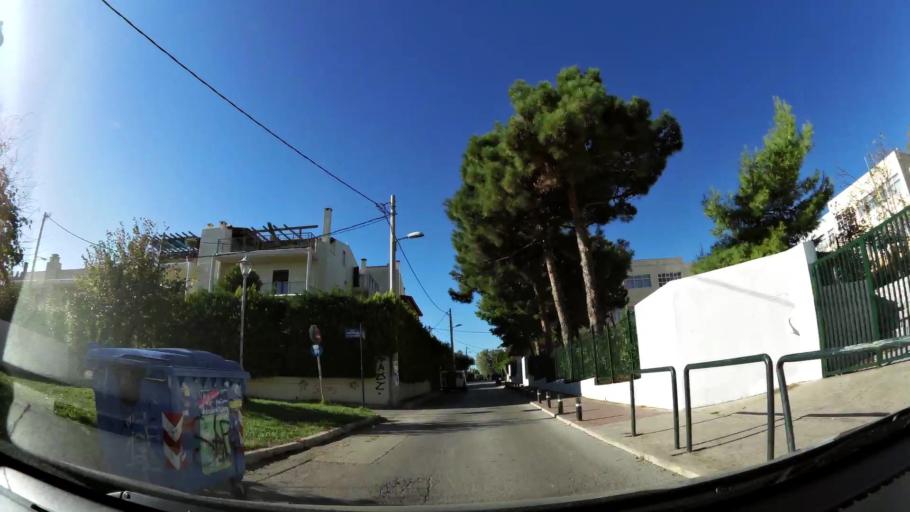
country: GR
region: Attica
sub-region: Nomarchia Athinas
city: Melissia
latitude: 38.0407
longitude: 23.8391
